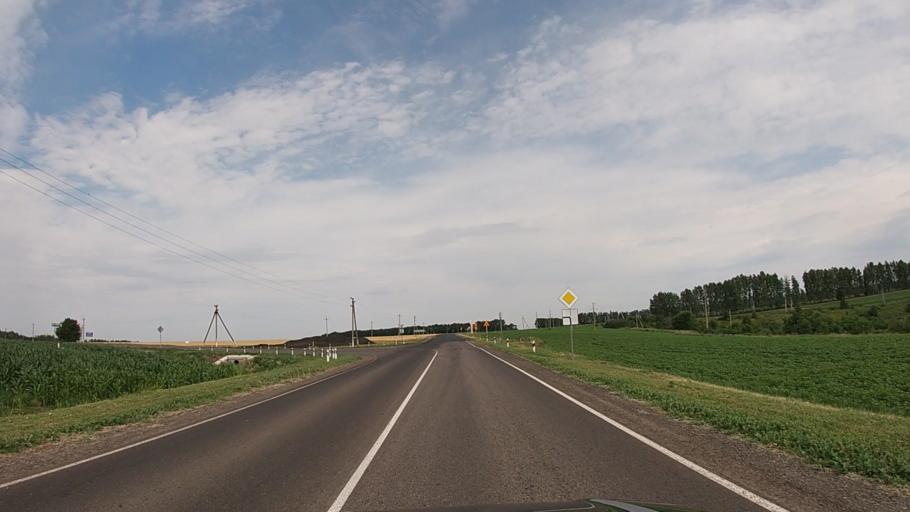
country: RU
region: Belgorod
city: Krasnaya Yaruga
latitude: 50.8332
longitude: 35.4898
